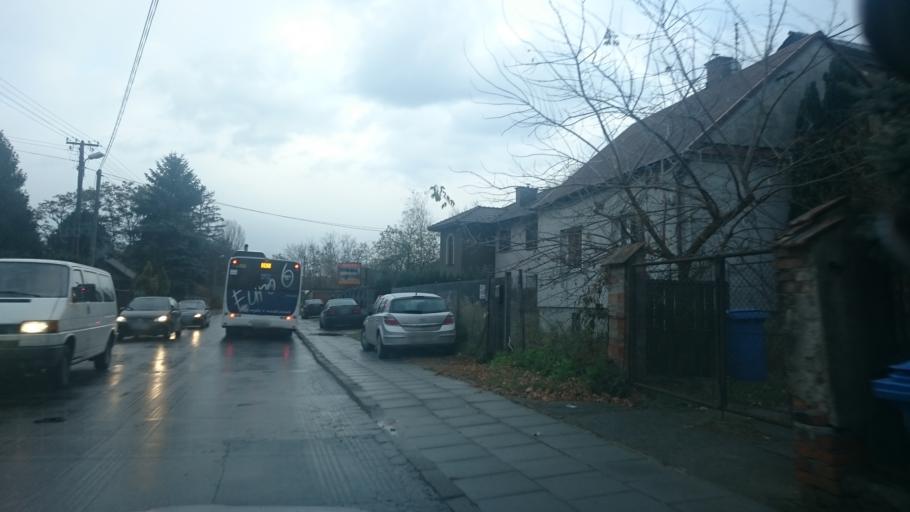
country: PL
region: Lesser Poland Voivodeship
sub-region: Powiat wielicki
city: Czarnochowice
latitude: 50.0225
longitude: 20.0048
